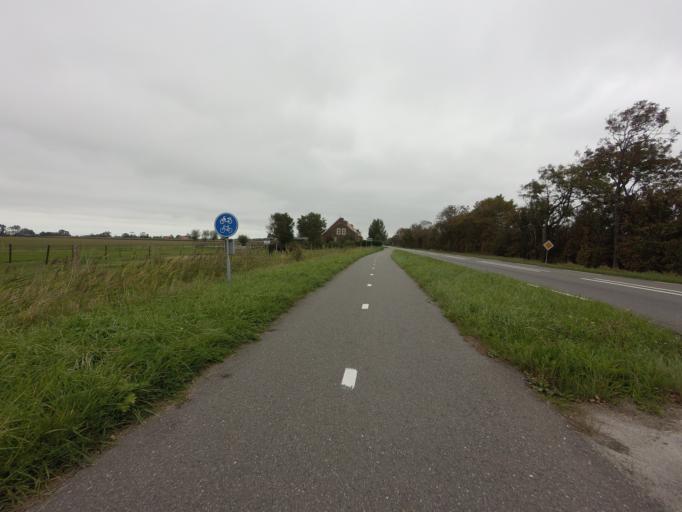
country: NL
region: Zeeland
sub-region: Gemeente Veere
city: Veere
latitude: 51.5231
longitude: 3.6418
